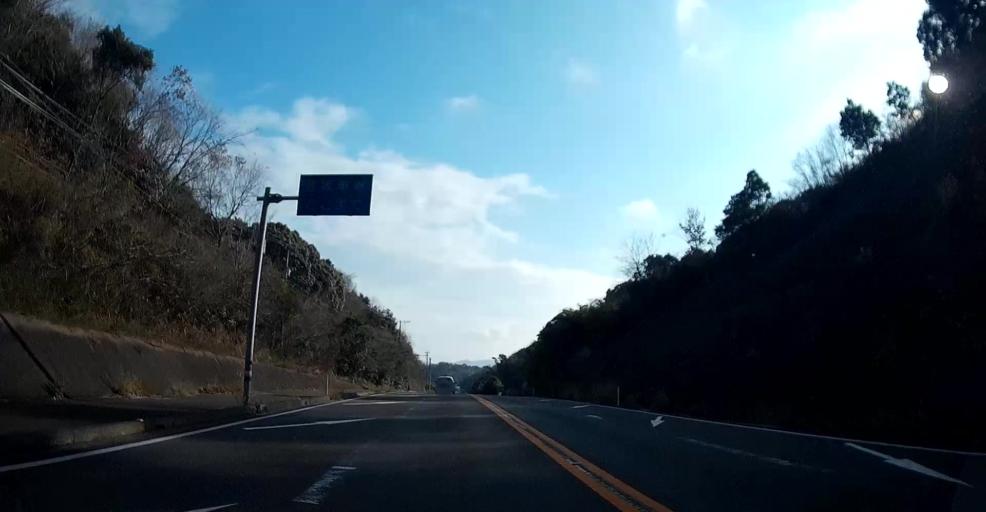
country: JP
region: Kumamoto
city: Yatsushiro
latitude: 32.5585
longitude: 130.4152
